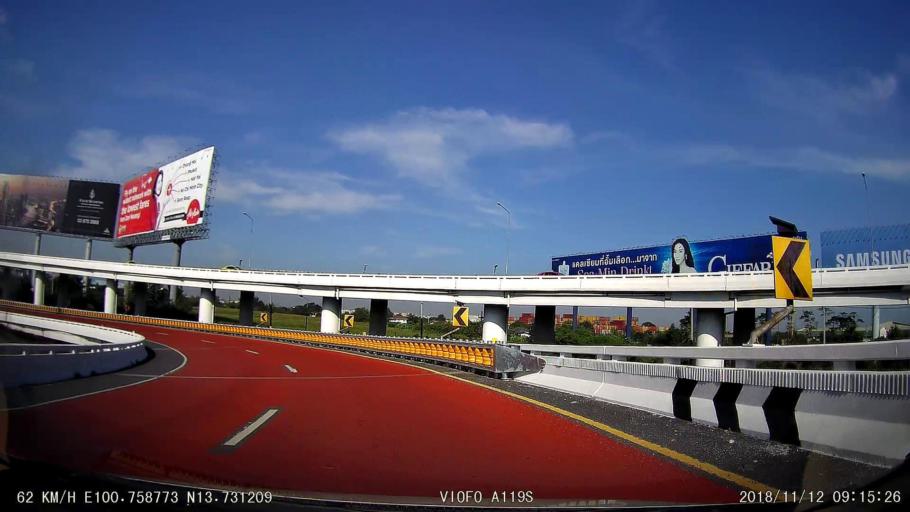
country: TH
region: Bangkok
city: Lat Krabang
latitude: 13.7313
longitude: 100.7585
